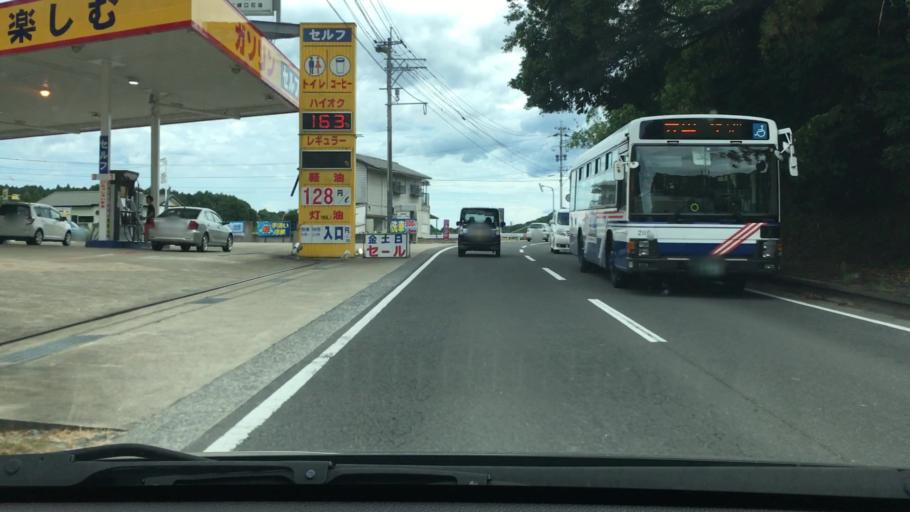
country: JP
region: Nagasaki
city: Togitsu
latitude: 32.9702
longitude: 129.7819
